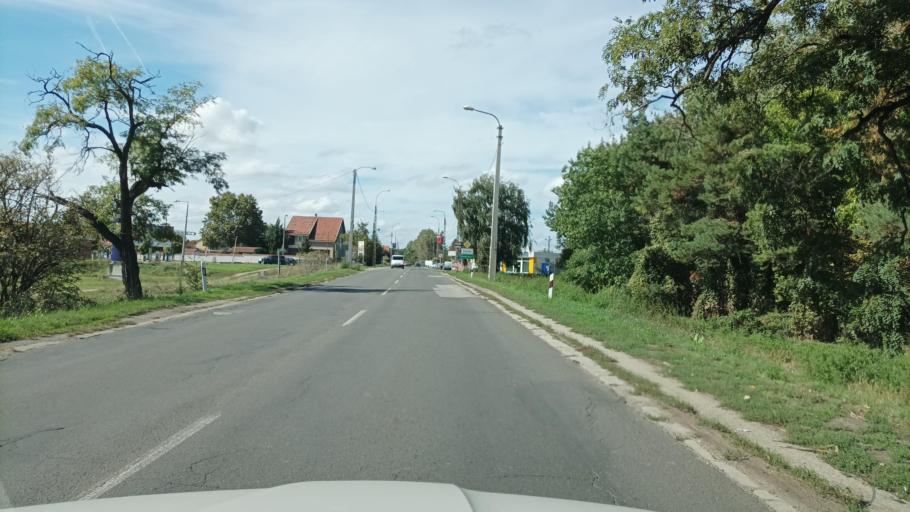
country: HU
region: Pest
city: Vecses
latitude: 47.4034
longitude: 19.2911
